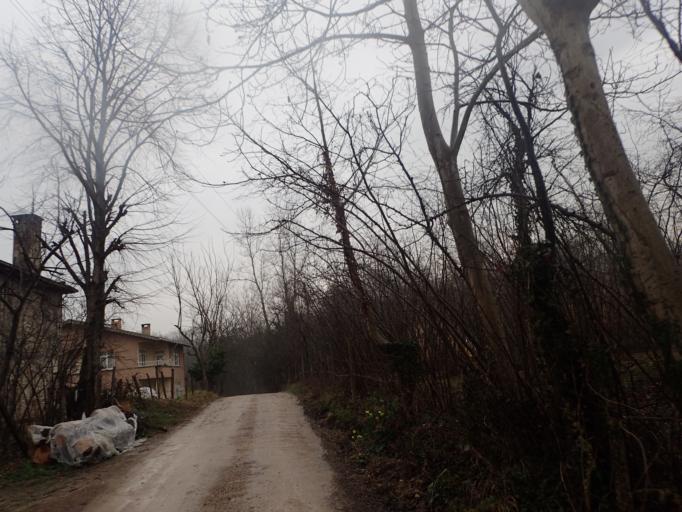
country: TR
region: Ordu
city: Camas
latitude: 40.9508
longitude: 37.5122
